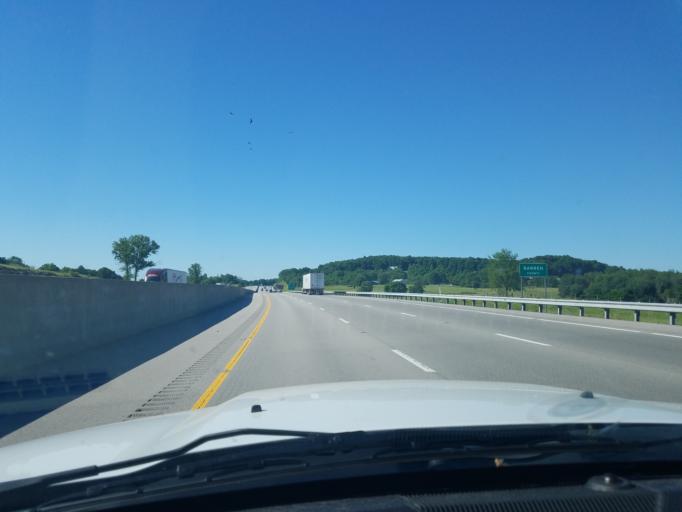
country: US
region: Kentucky
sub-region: Barren County
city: Cave City
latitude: 37.1565
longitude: -85.9711
